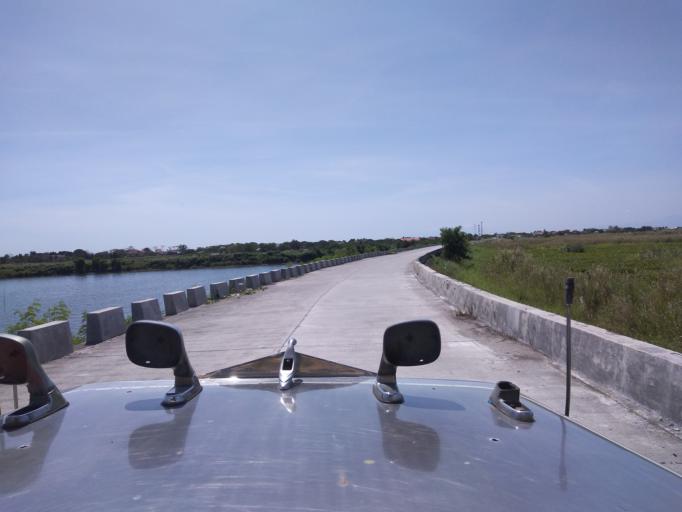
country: PH
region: Central Luzon
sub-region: Province of Pampanga
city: Minalin
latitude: 14.9864
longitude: 120.6941
